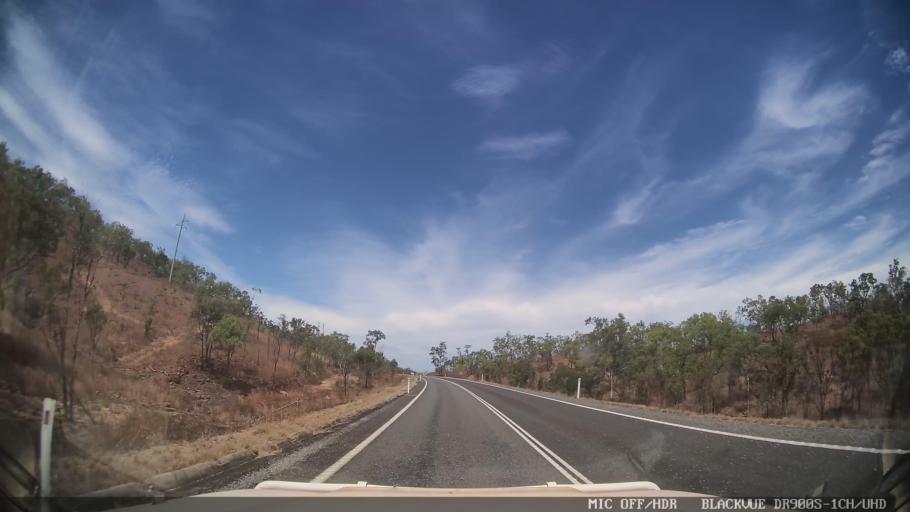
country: AU
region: Queensland
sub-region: Cook
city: Cooktown
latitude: -15.7033
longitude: 145.0257
